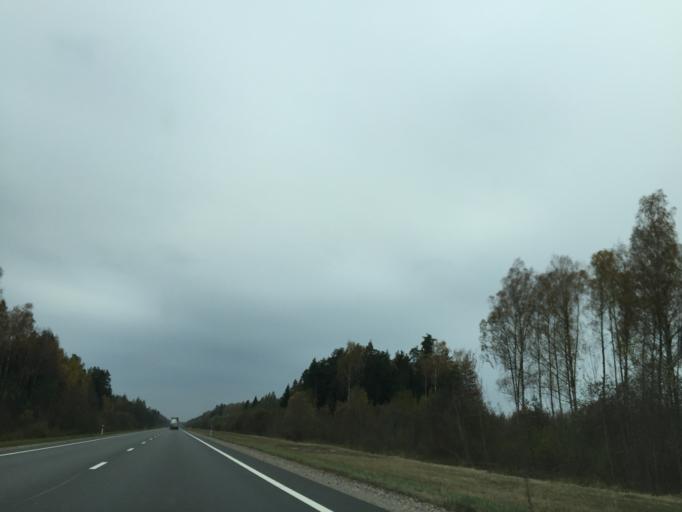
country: LV
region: Ozolnieku
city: Ozolnieki
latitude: 56.7208
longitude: 23.8495
